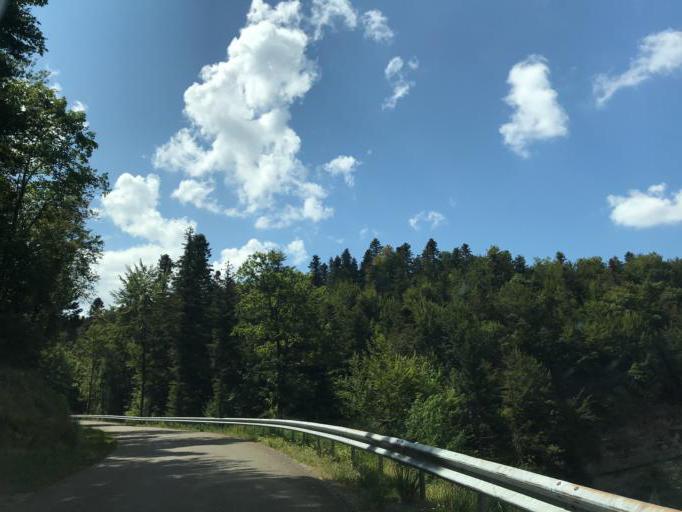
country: FR
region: Franche-Comte
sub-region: Departement du Jura
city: Moirans-en-Montagne
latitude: 46.4964
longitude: 5.7739
